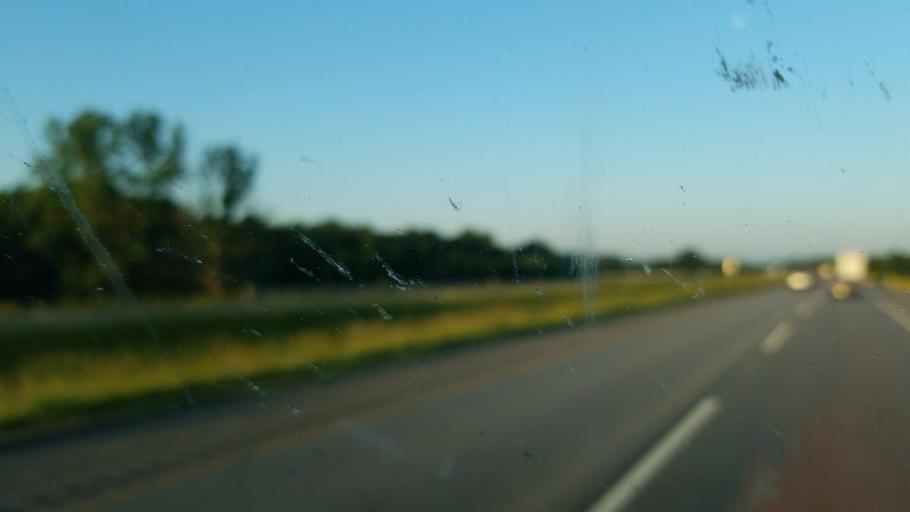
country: US
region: Indiana
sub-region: LaPorte County
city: LaPorte
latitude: 41.6471
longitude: -86.7741
